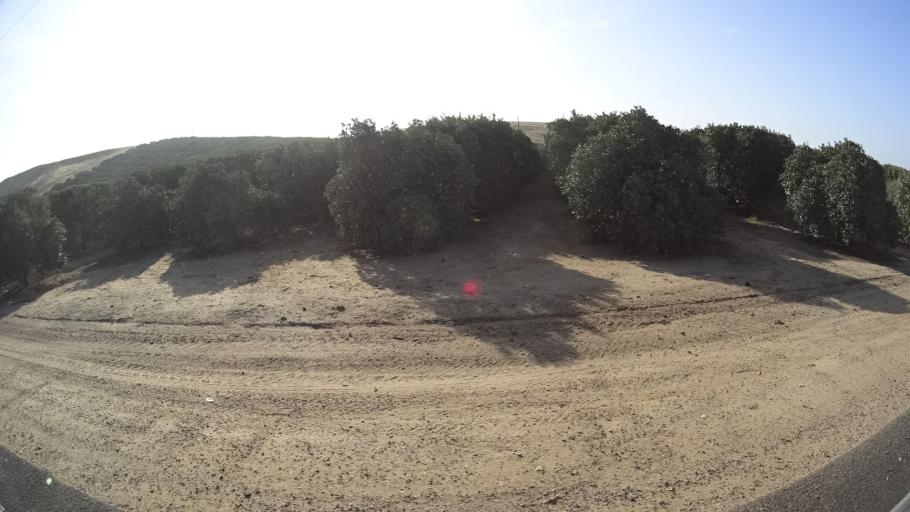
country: US
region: California
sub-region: Tulare County
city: Richgrove
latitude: 35.6616
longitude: -119.0917
